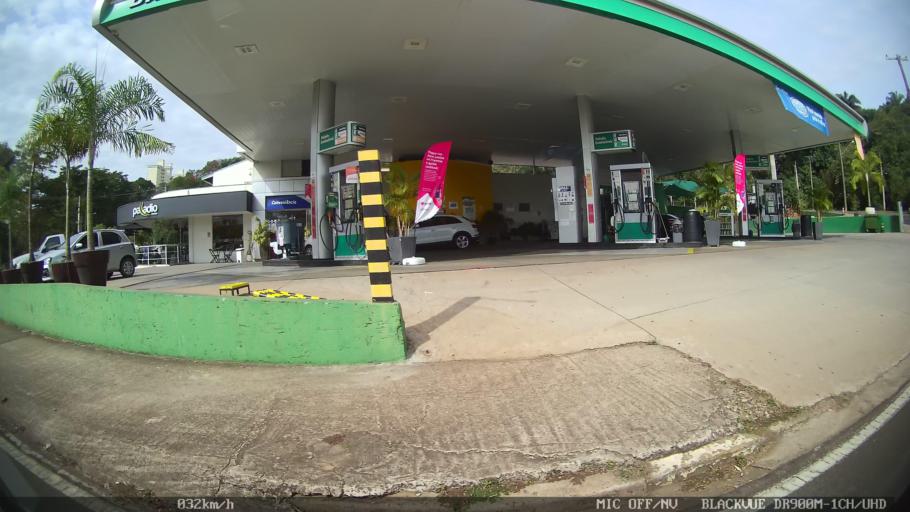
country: BR
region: Sao Paulo
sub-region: Piracicaba
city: Piracicaba
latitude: -22.7277
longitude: -47.6612
